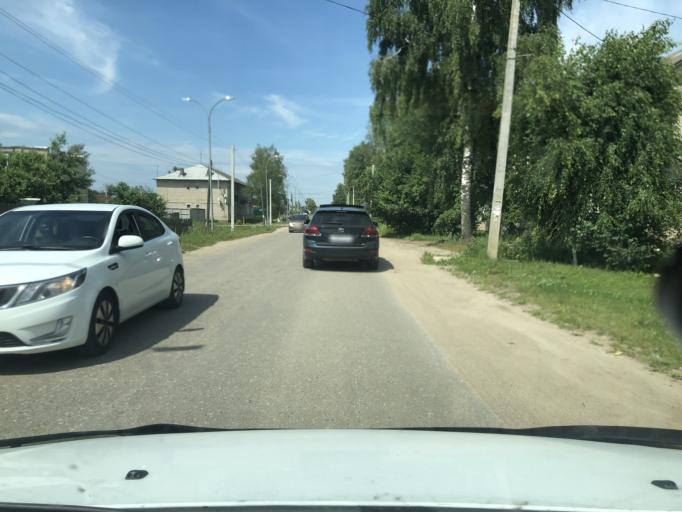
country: RU
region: Jaroslavl
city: Petrovsk
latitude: 57.0116
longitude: 39.2681
